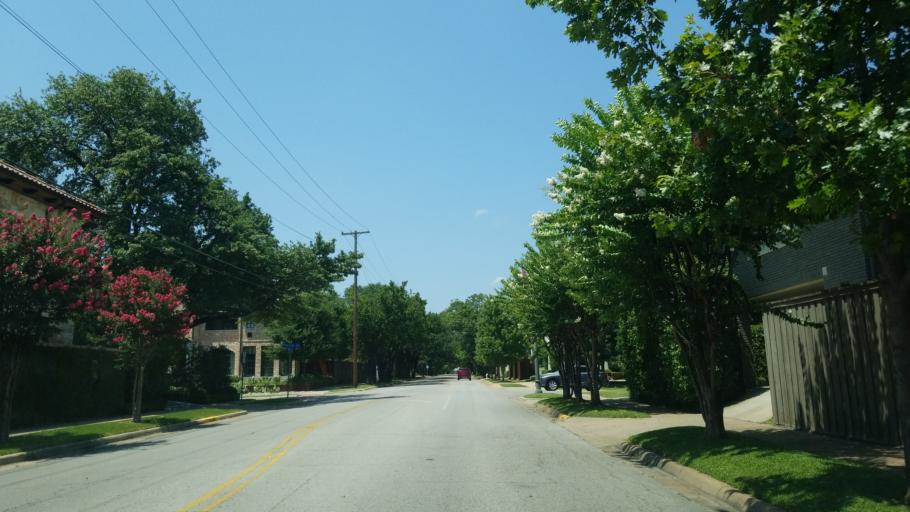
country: US
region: Texas
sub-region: Dallas County
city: Highland Park
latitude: 32.8307
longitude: -96.7871
